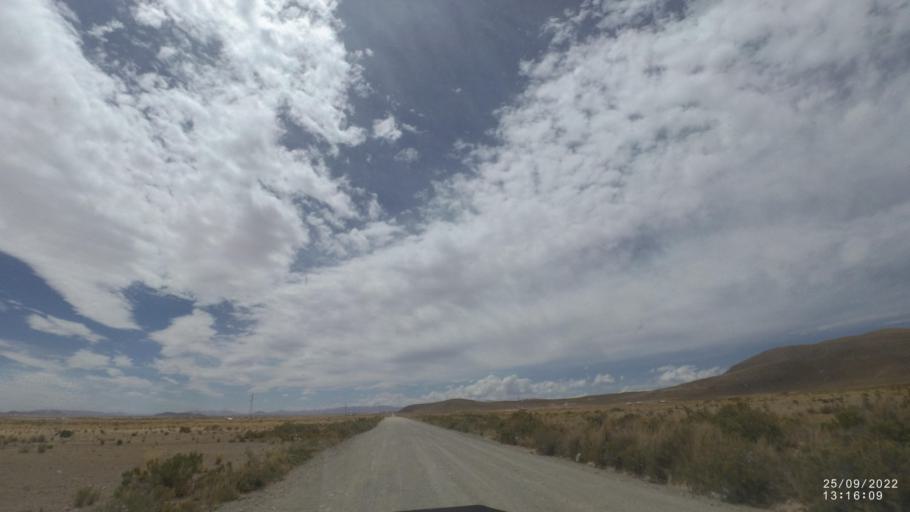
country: BO
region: Oruro
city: Oruro
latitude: -17.9213
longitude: -67.0422
